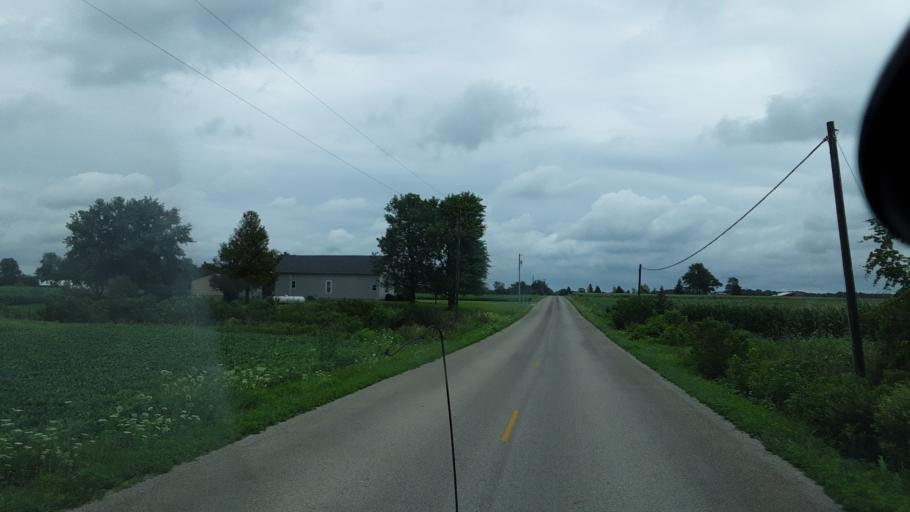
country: US
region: Indiana
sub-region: Jay County
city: Portland
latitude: 40.4822
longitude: -85.0090
